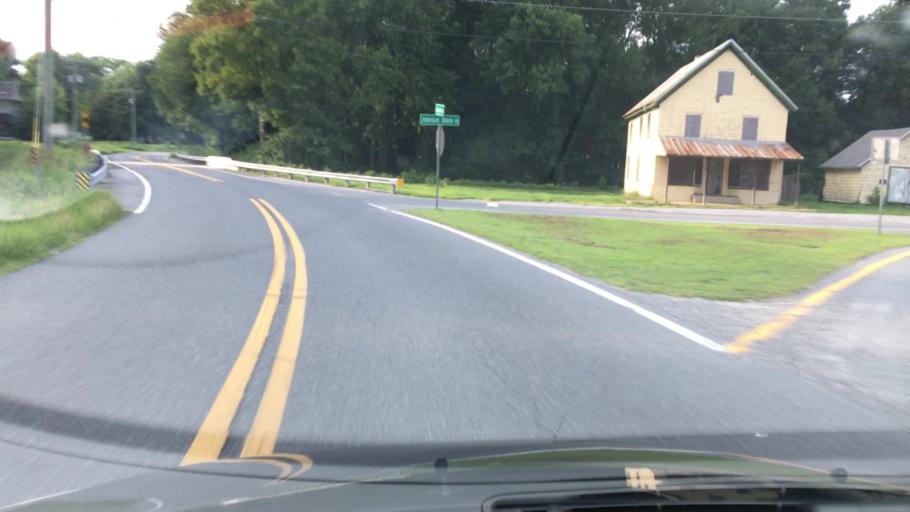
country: US
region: Maryland
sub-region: Worcester County
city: Ocean Pines
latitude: 38.4750
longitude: -75.1392
